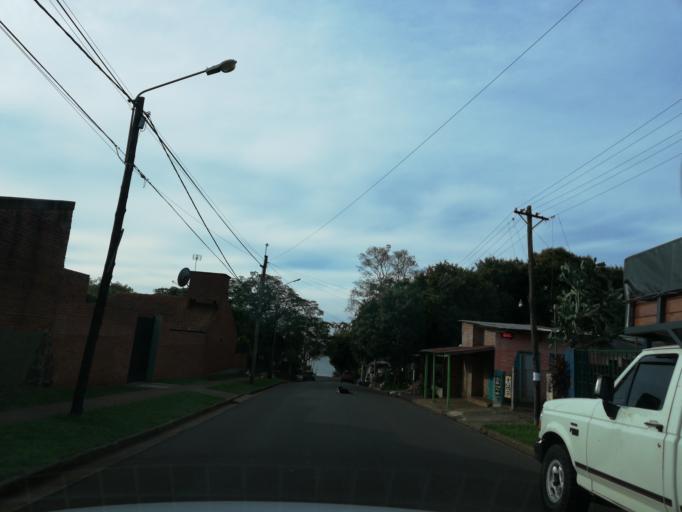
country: AR
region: Misiones
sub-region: Departamento de Capital
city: Posadas
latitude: -27.3574
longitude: -55.9190
